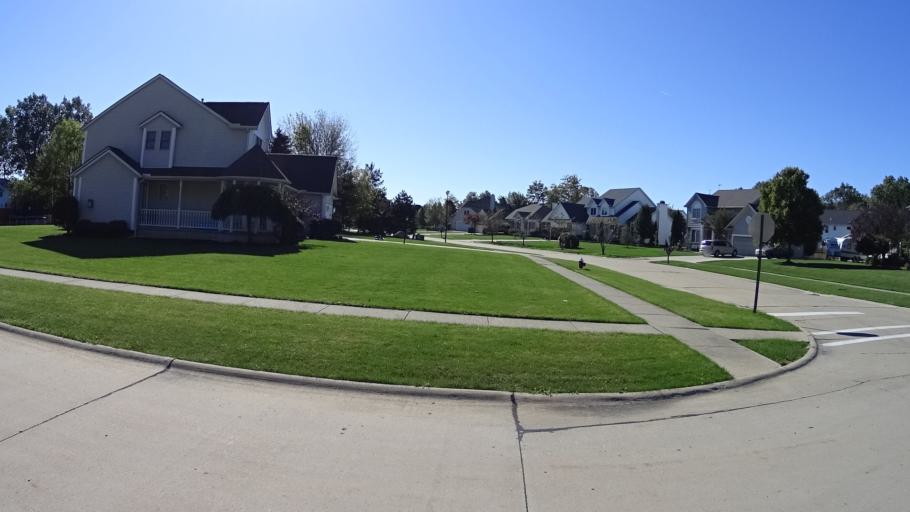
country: US
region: Ohio
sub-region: Lorain County
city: Amherst
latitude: 41.4095
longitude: -82.2464
